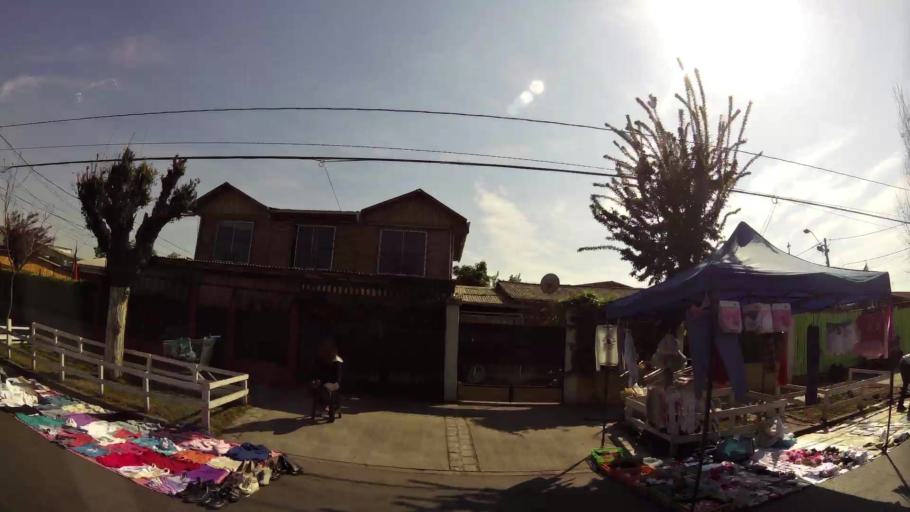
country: CL
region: Santiago Metropolitan
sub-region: Provincia de Santiago
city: La Pintana
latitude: -33.5620
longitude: -70.6593
